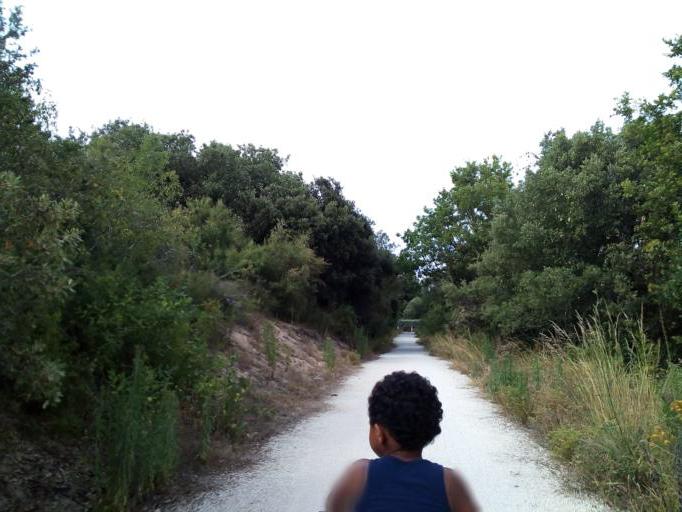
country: FR
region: Poitou-Charentes
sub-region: Departement de la Charente-Maritime
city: Boyard-Ville
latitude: 45.9566
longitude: -1.2447
